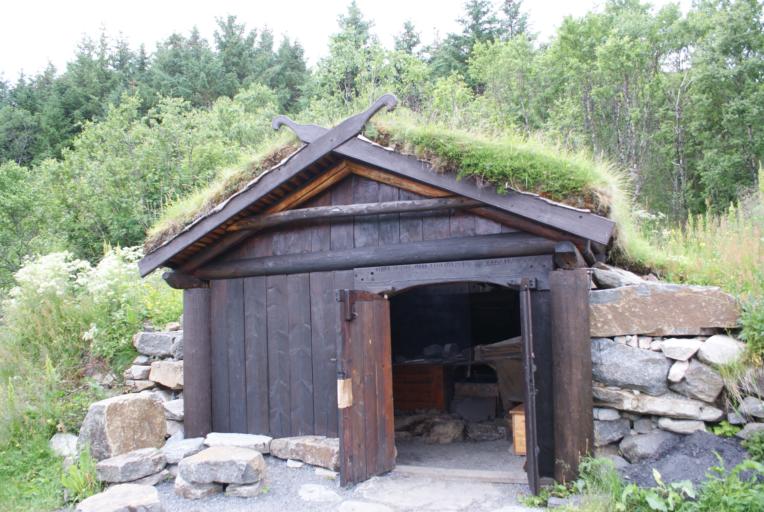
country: NO
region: Nordland
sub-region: Vestvagoy
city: Evjen
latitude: 68.2438
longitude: 13.7799
